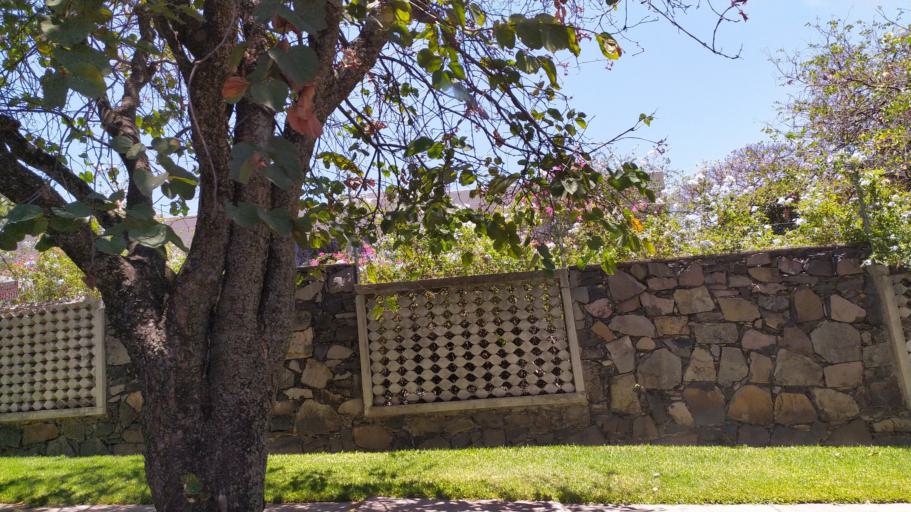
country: MX
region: Jalisco
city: Guadalajara
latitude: 20.6894
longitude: -103.4025
